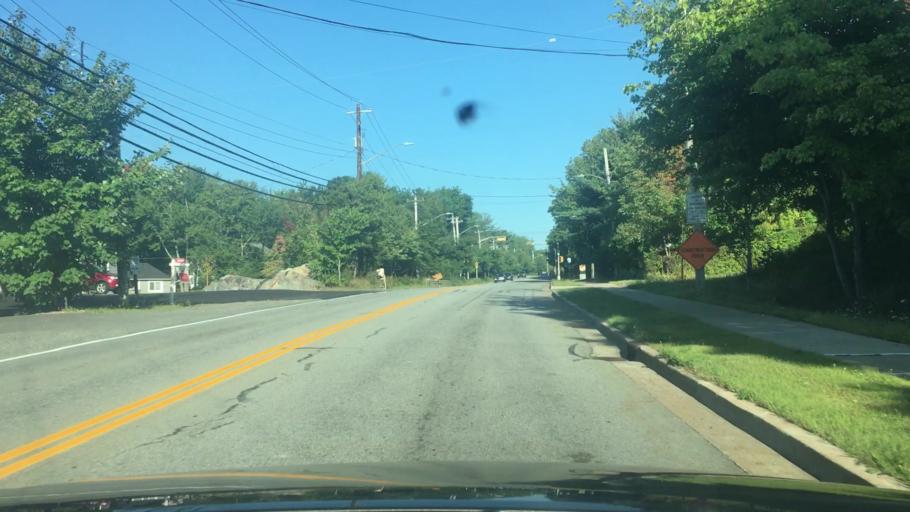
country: CA
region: Nova Scotia
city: Dartmouth
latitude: 44.7163
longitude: -63.6817
